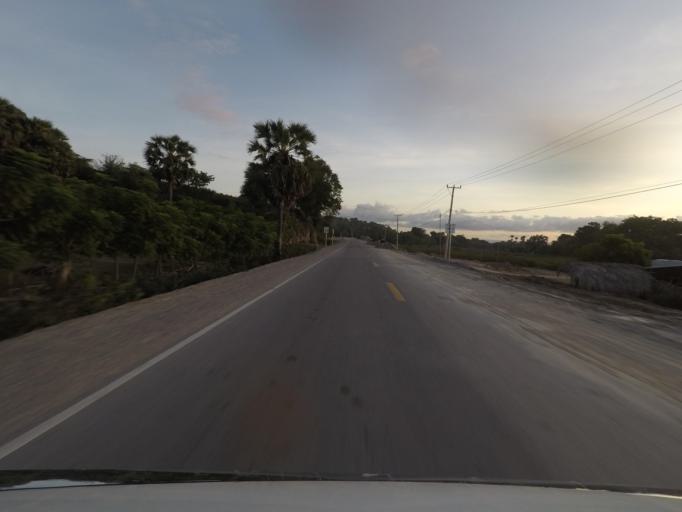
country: TL
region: Baucau
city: Baucau
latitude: -8.4673
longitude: 126.6044
